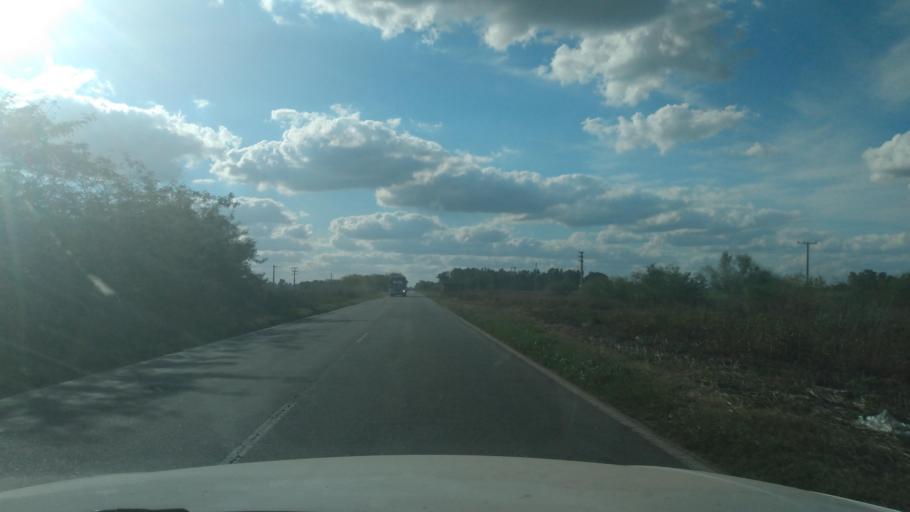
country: AR
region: Buenos Aires
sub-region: Partido de Mercedes
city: Mercedes
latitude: -34.7595
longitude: -59.3765
